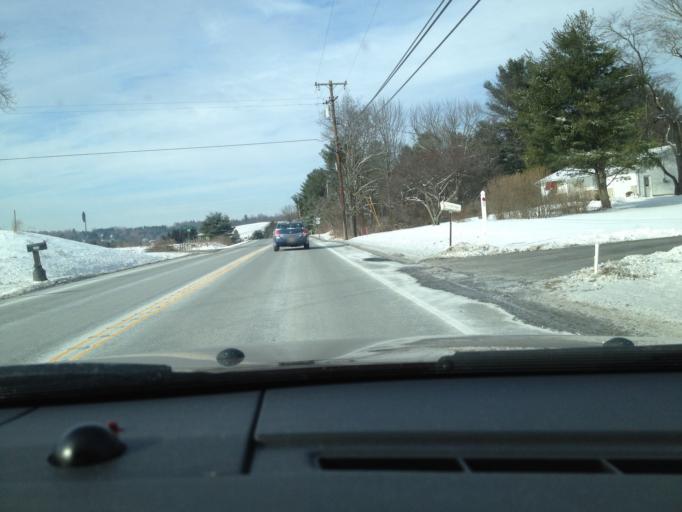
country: US
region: New York
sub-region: Rensselaer County
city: West Sand Lake
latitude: 42.6509
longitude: -73.6526
